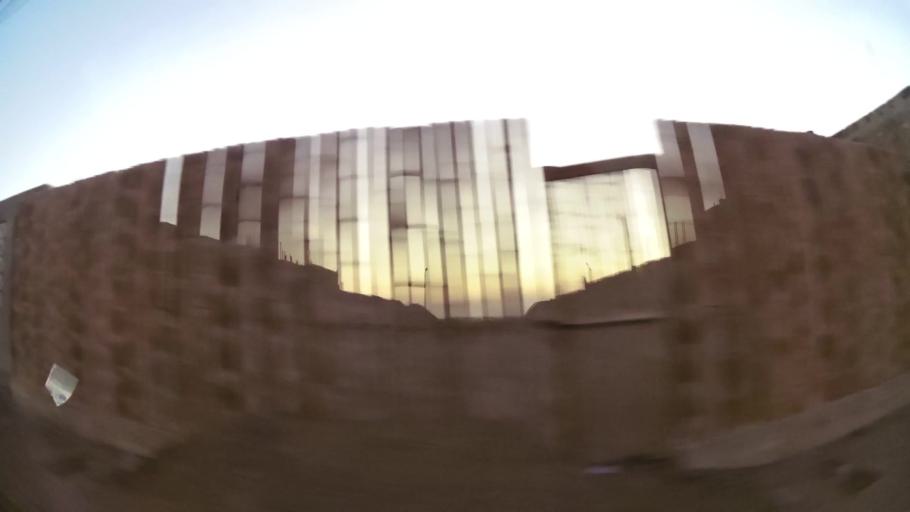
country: PE
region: Ica
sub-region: Provincia de Pisco
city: Pisco
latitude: -13.7123
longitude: -76.2186
